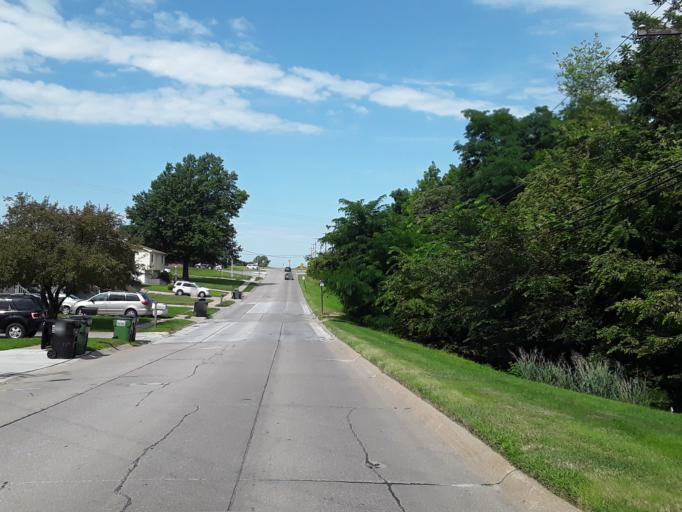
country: US
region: Nebraska
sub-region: Cass County
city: Plattsmouth
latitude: 41.0025
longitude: -95.9032
